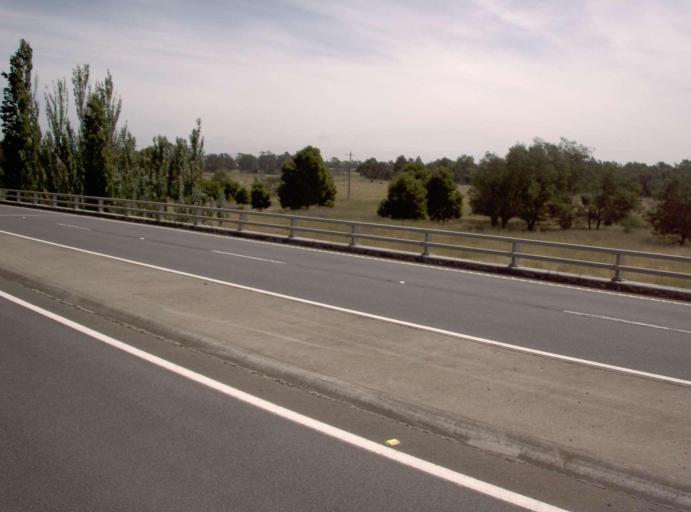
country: AU
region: Victoria
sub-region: Wellington
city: Heyfield
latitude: -38.1435
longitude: 146.7922
